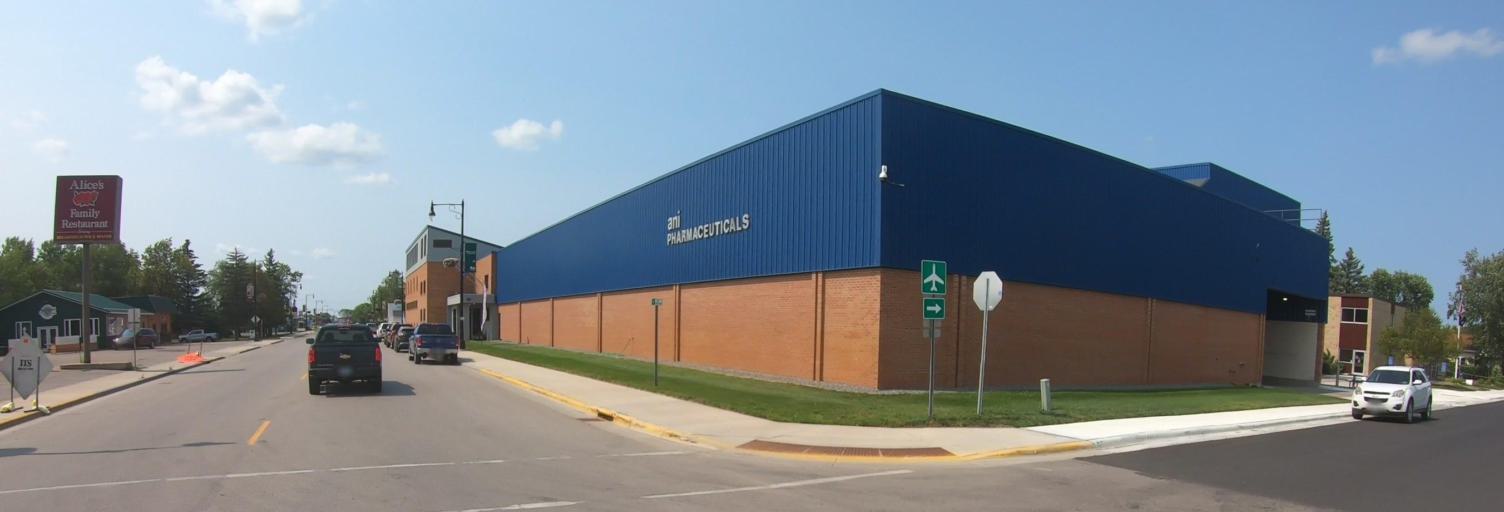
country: US
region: Minnesota
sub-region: Lake of the Woods County
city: Baudette
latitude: 48.7131
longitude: -94.6001
